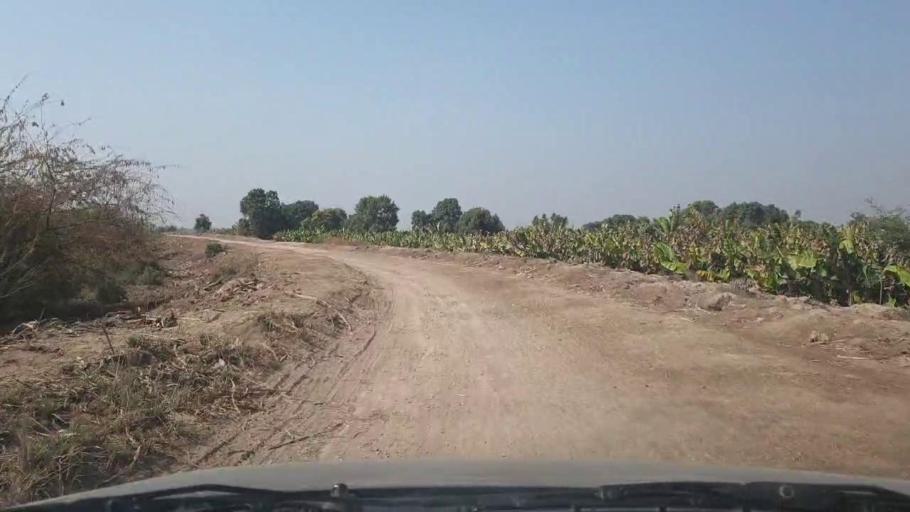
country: PK
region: Sindh
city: Mirwah Gorchani
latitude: 25.2478
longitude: 69.1047
